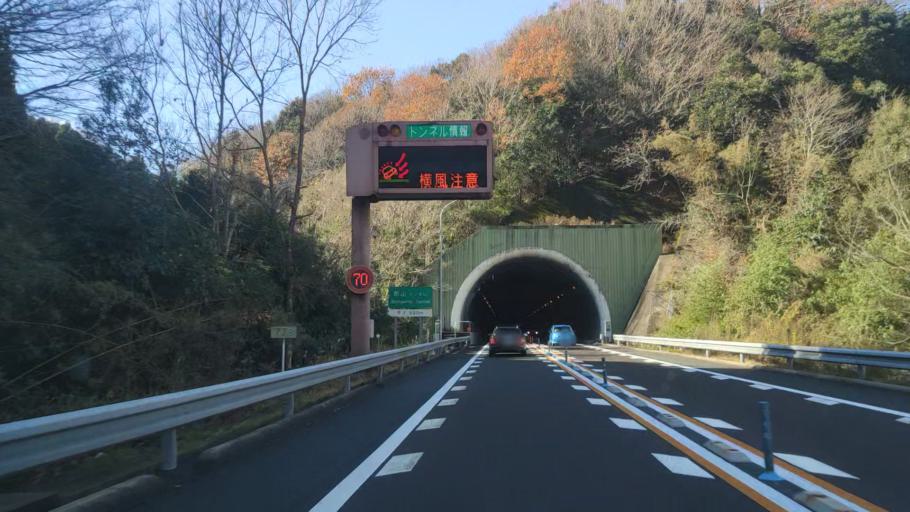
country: JP
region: Tokushima
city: Ikedacho
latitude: 34.0221
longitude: 133.7993
